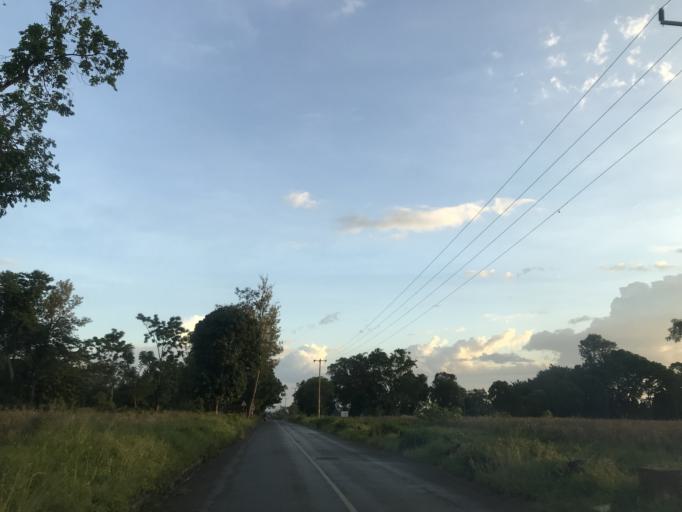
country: TZ
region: Arusha
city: Usa River
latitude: -3.3585
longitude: 36.8664
